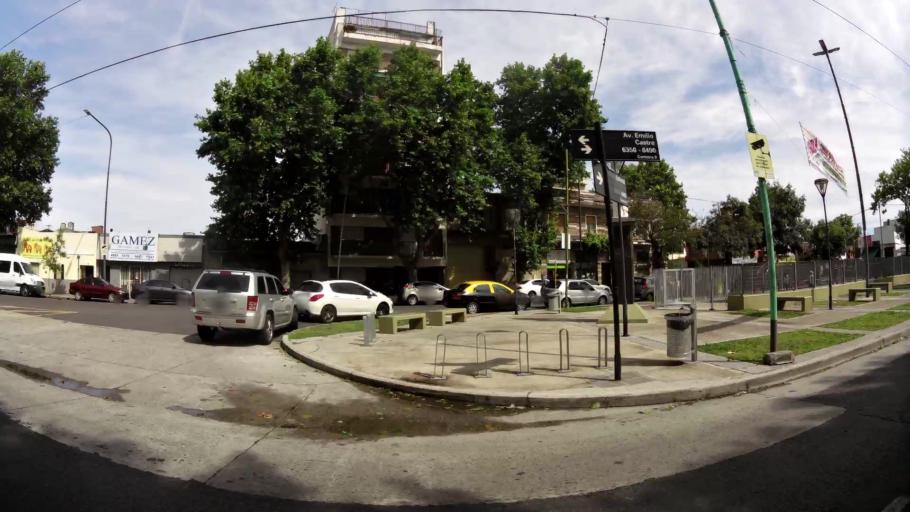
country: AR
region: Buenos Aires F.D.
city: Villa Lugano
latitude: -34.6501
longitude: -58.5112
